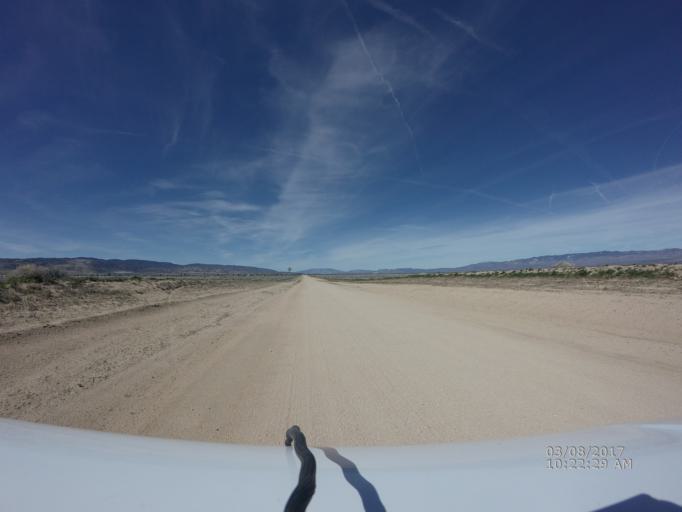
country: US
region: California
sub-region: Los Angeles County
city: Green Valley
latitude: 34.7604
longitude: -118.4320
